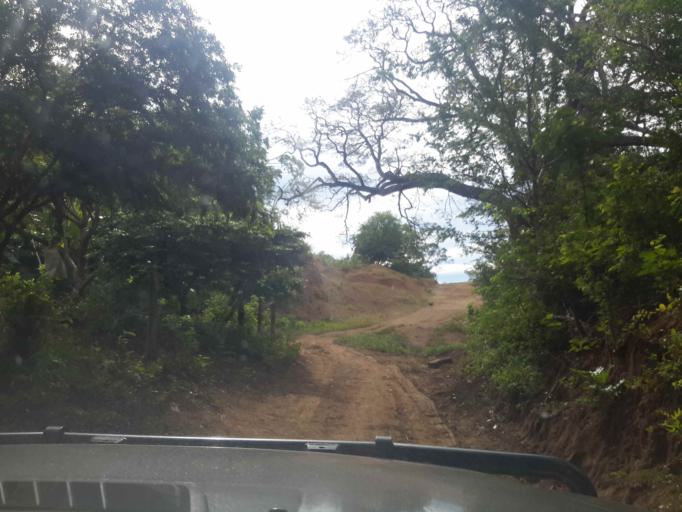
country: NI
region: Carazo
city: Santa Teresa
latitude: 11.6742
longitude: -86.3048
